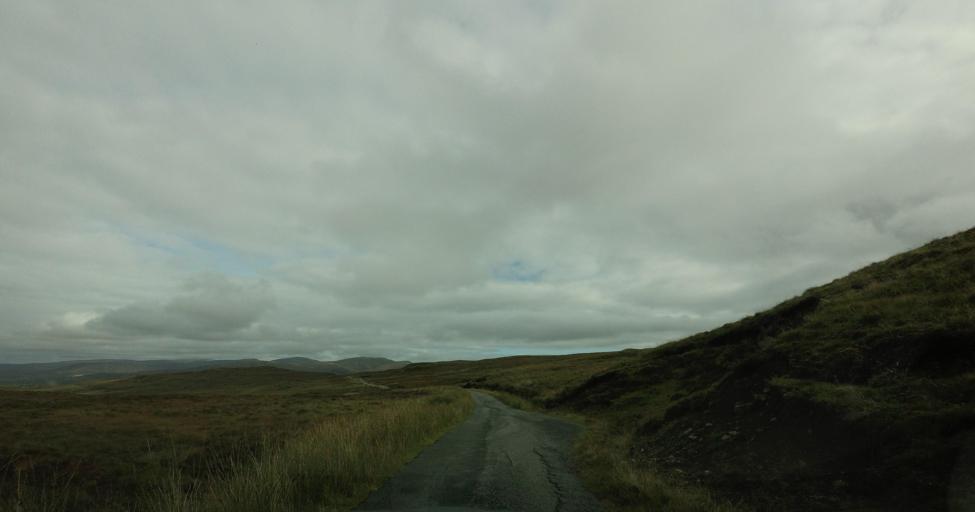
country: GB
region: Scotland
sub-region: Highland
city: Isle of Skye
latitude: 57.4014
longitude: -6.2698
